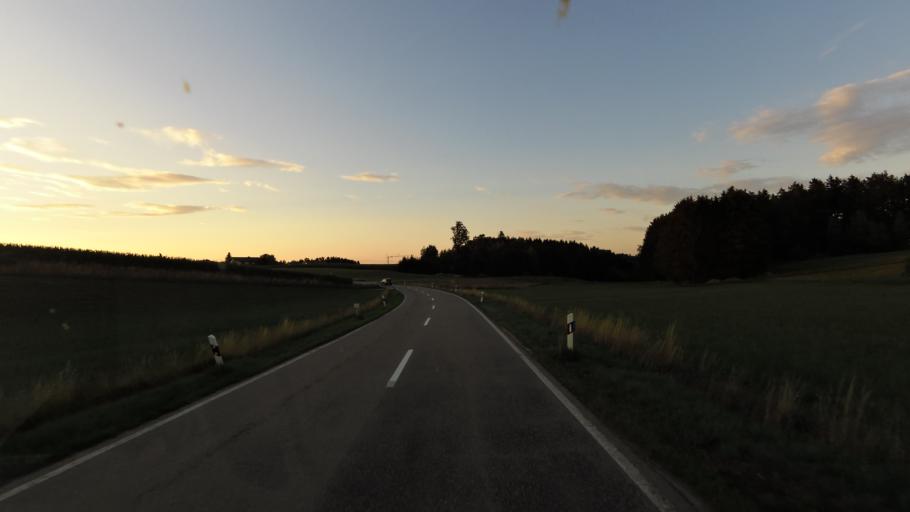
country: DE
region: Bavaria
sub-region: Upper Bavaria
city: Taufkirchen
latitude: 48.1250
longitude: 12.4636
